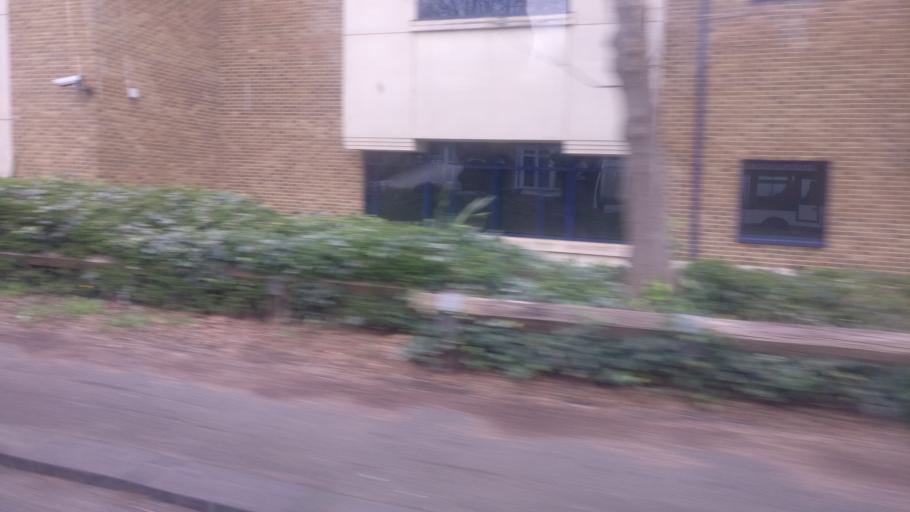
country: GB
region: England
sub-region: Surrey
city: Chertsey
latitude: 51.3873
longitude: -0.5056
